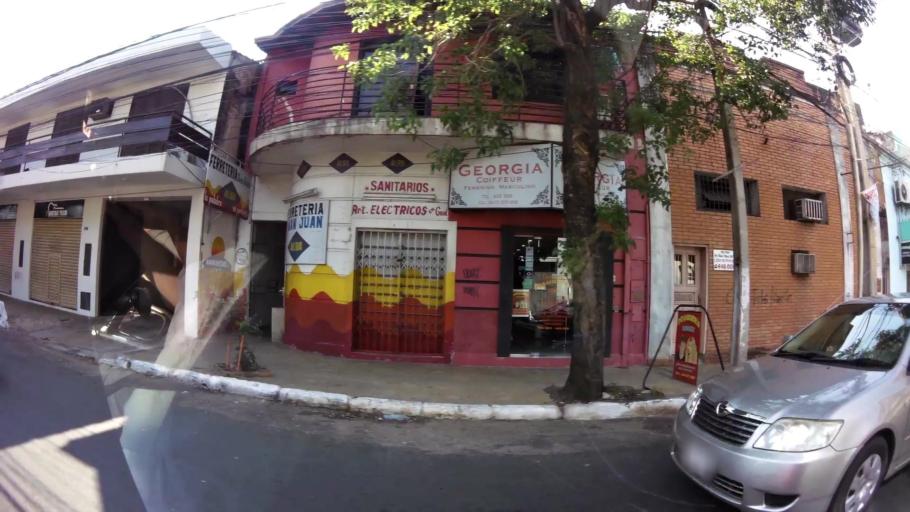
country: PY
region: Asuncion
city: Asuncion
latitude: -25.2927
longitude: -57.6300
